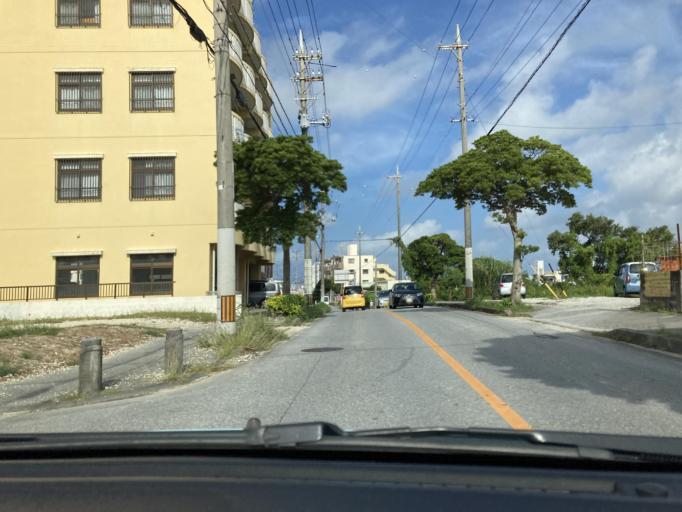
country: JP
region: Okinawa
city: Ginowan
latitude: 26.2549
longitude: 127.7724
